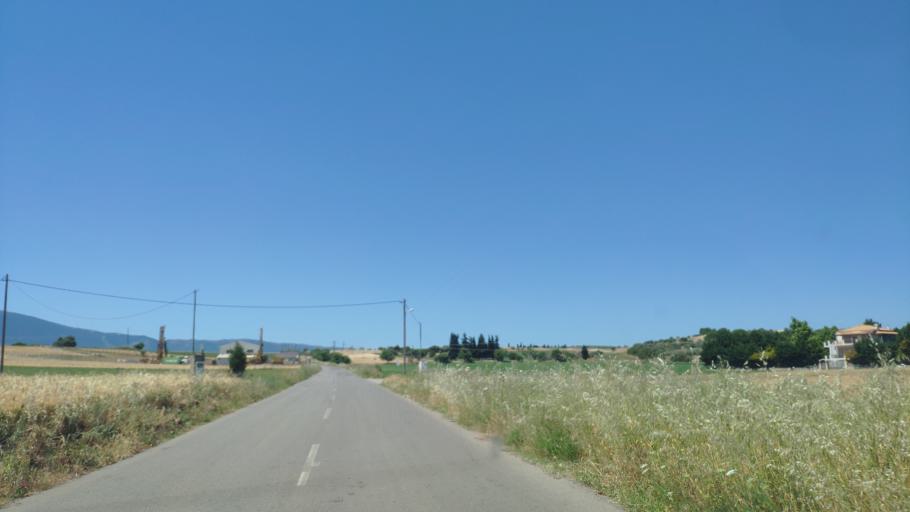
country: GR
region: Central Greece
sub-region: Nomos Voiotias
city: Thivai
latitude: 38.2972
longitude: 23.3055
